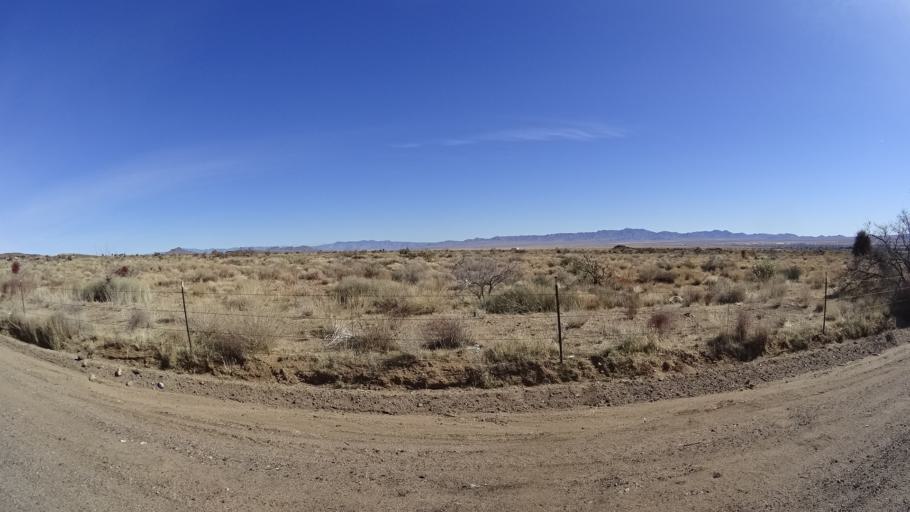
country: US
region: Arizona
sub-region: Mohave County
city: New Kingman-Butler
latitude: 35.2770
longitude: -114.0490
